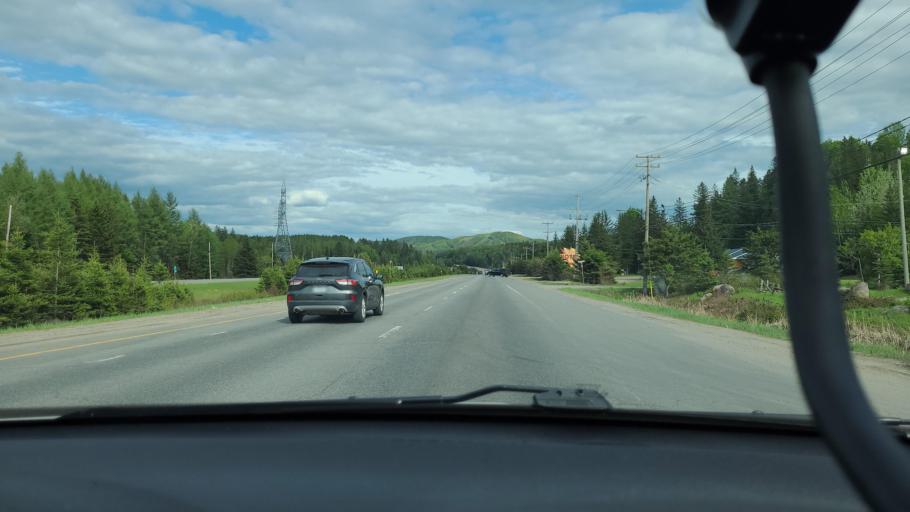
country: CA
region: Quebec
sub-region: Laurentides
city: Mont-Tremblant
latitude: 46.1159
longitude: -74.5511
